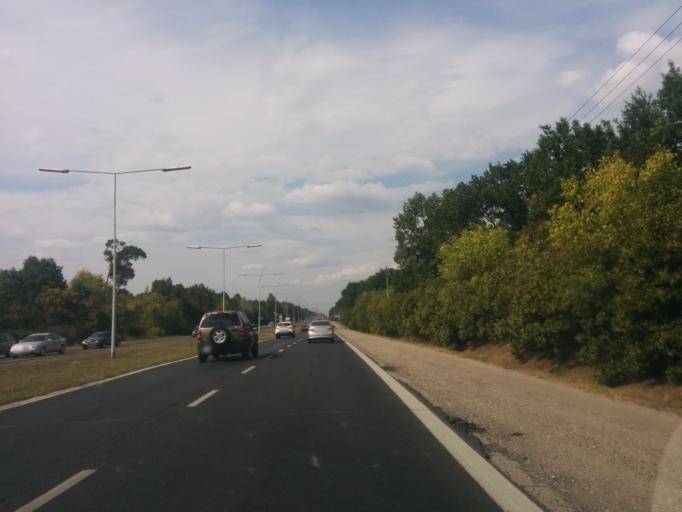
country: PL
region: Masovian Voivodeship
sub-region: Warszawa
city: Bielany
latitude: 52.3108
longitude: 20.9253
